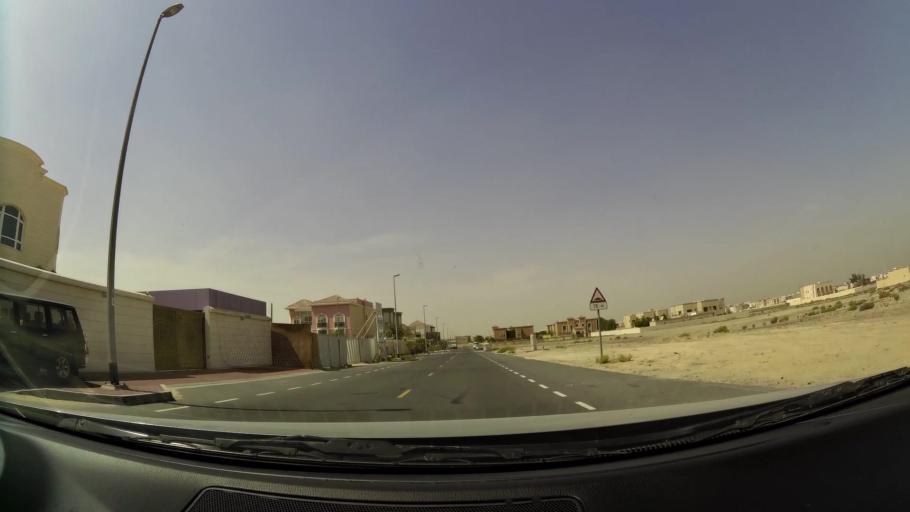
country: AE
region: Ash Shariqah
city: Sharjah
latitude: 25.1862
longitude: 55.4321
